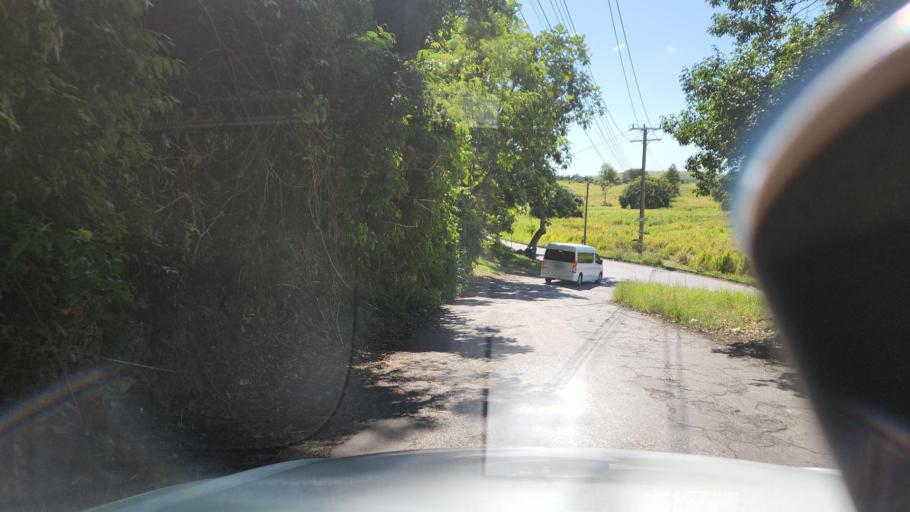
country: BB
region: Saint Thomas
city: Welchman Hall
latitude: 13.1877
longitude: -59.5958
